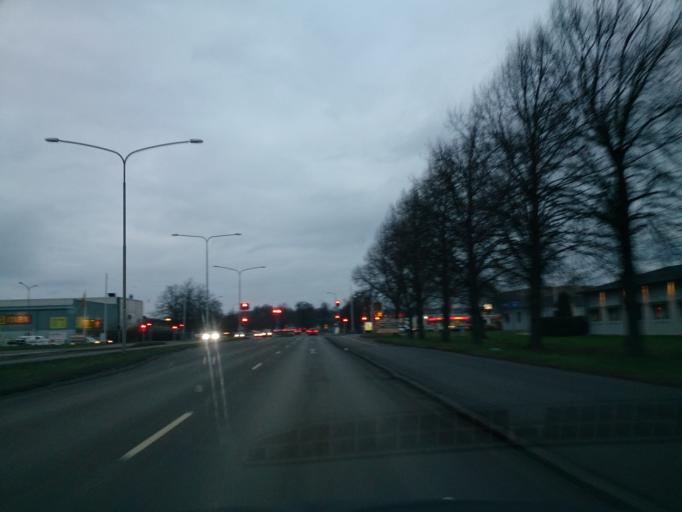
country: SE
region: OEstergoetland
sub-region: Norrkopings Kommun
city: Norrkoping
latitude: 58.6012
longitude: 16.1879
